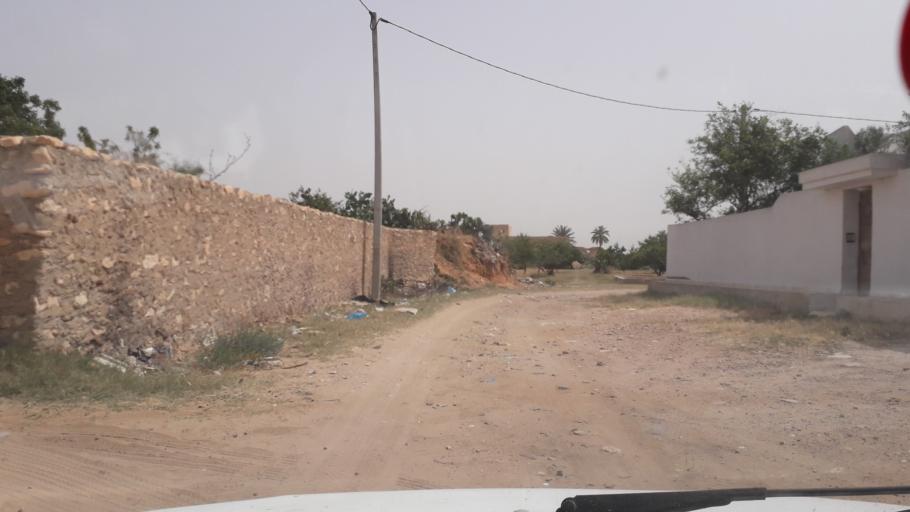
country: TN
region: Safaqis
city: Al Qarmadah
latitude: 34.8106
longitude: 10.7729
